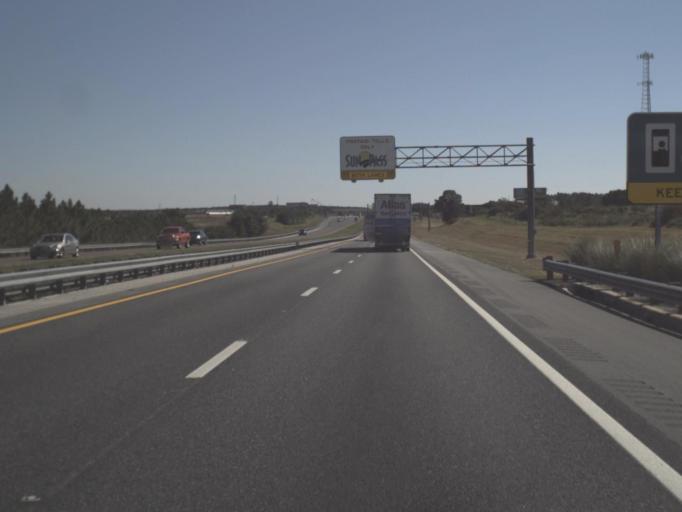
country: US
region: Florida
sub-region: Lake County
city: Yalaha
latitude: 28.6739
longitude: -81.8508
